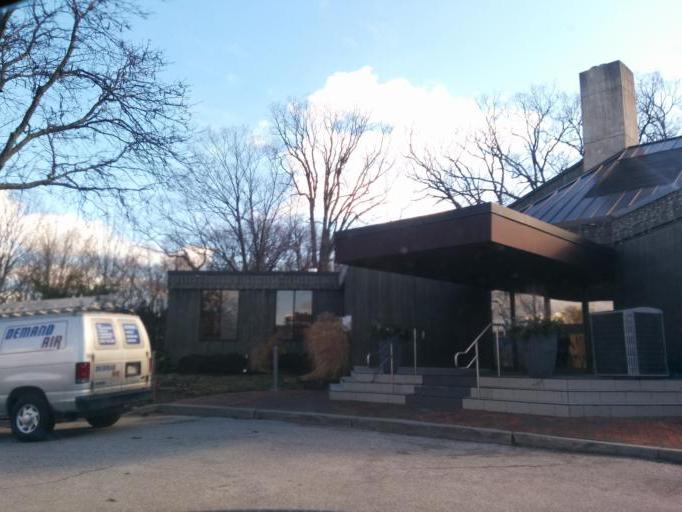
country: CA
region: Ontario
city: Mississauga
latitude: 43.5516
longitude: -79.6443
